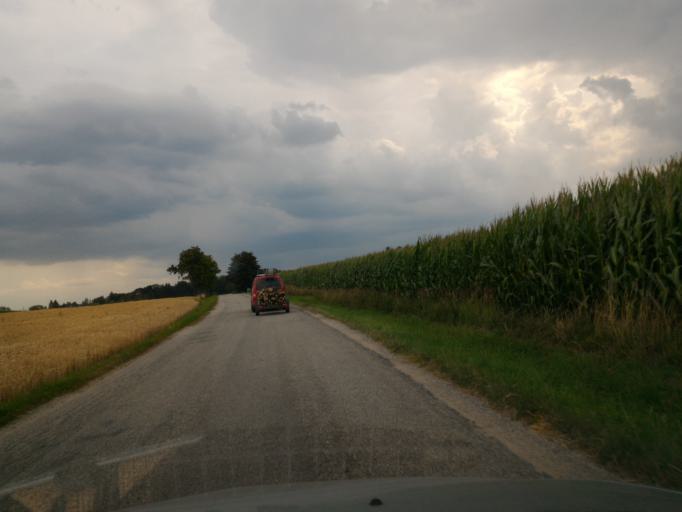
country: CZ
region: Vysocina
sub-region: Okres Jihlava
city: Telc
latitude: 49.2291
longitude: 15.4249
